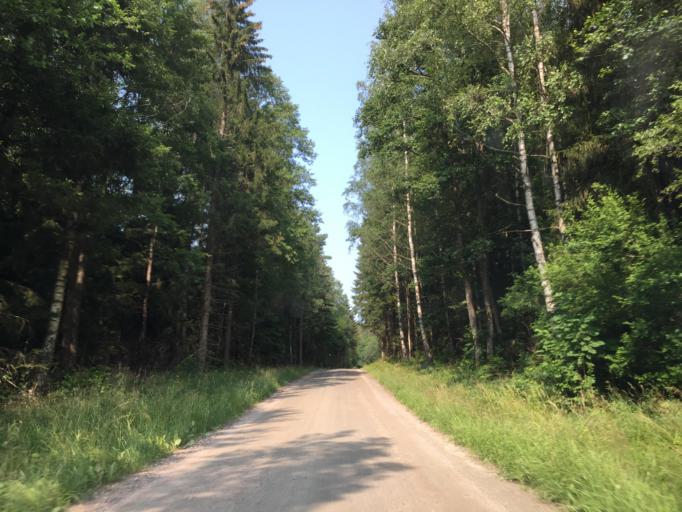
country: SE
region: Vaestra Goetaland
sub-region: Trollhattan
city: Sjuntorp
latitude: 58.2658
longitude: 12.1024
